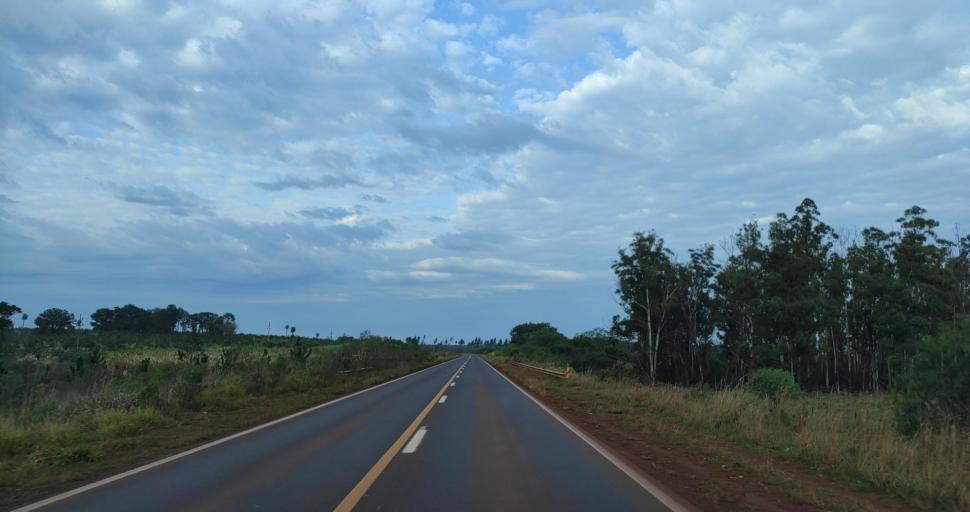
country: AR
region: Corrientes
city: San Carlos
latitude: -27.8735
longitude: -55.9313
